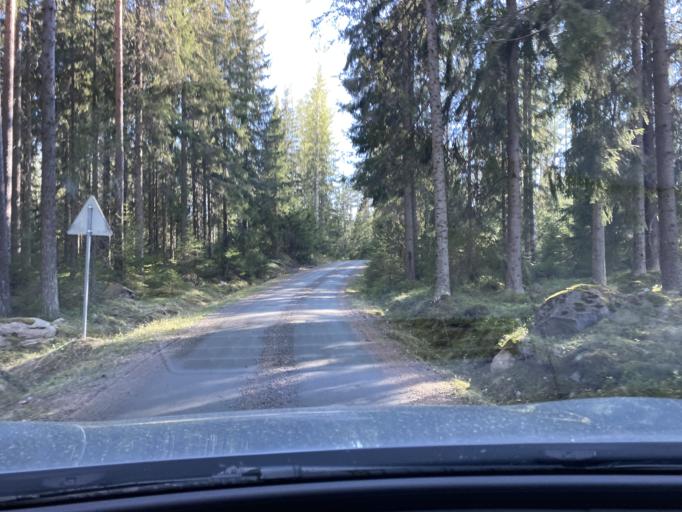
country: FI
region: Pirkanmaa
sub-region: Lounais-Pirkanmaa
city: Punkalaidun
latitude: 61.0284
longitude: 23.2166
